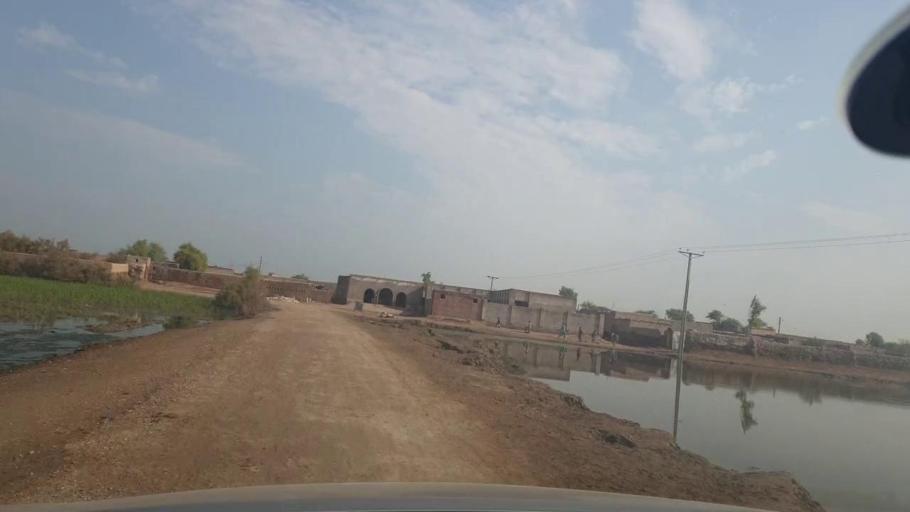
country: PK
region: Balochistan
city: Mehrabpur
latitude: 28.0730
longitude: 68.2110
